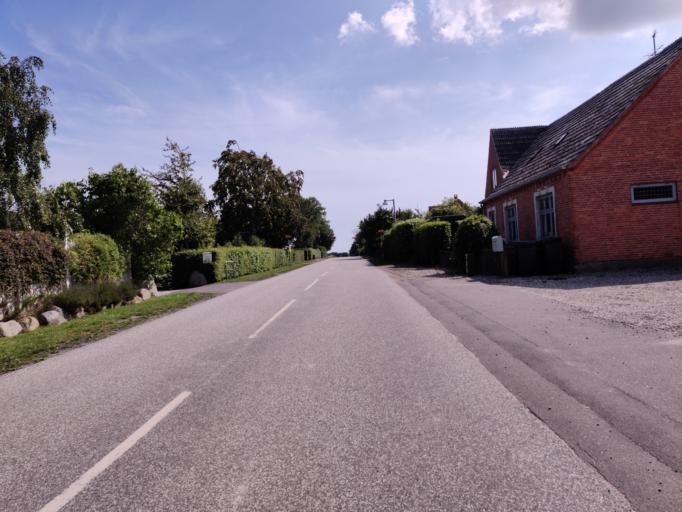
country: DK
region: Zealand
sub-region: Guldborgsund Kommune
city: Nykobing Falster
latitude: 54.6321
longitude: 11.9047
